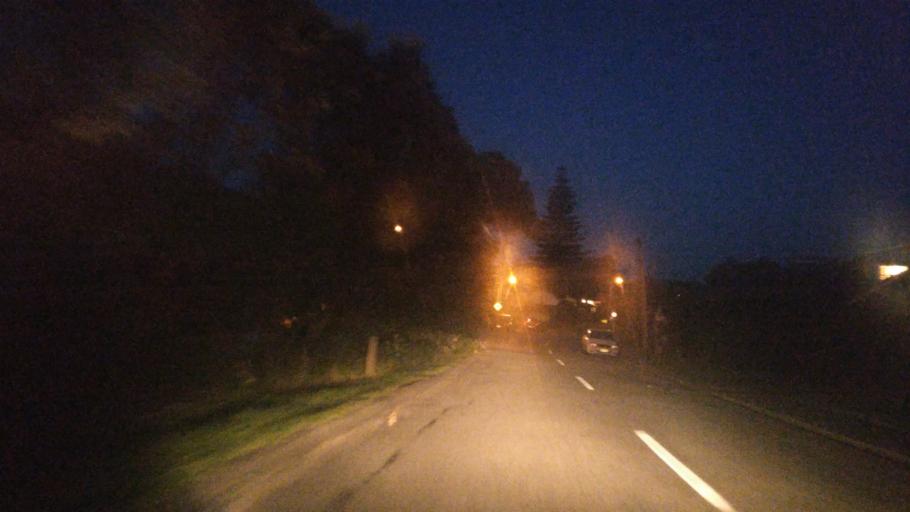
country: NZ
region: Wellington
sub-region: Kapiti Coast District
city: Paraparaumu
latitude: -40.9920
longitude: 174.9469
